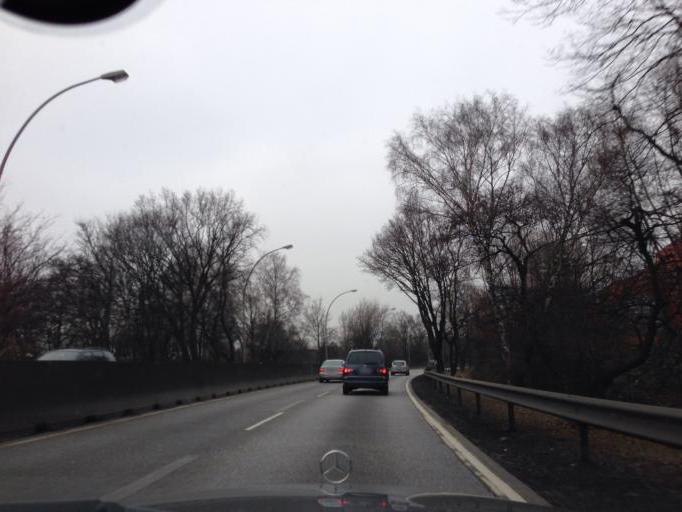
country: DE
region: Hamburg
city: Kleiner Grasbrook
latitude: 53.5106
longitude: 9.9995
